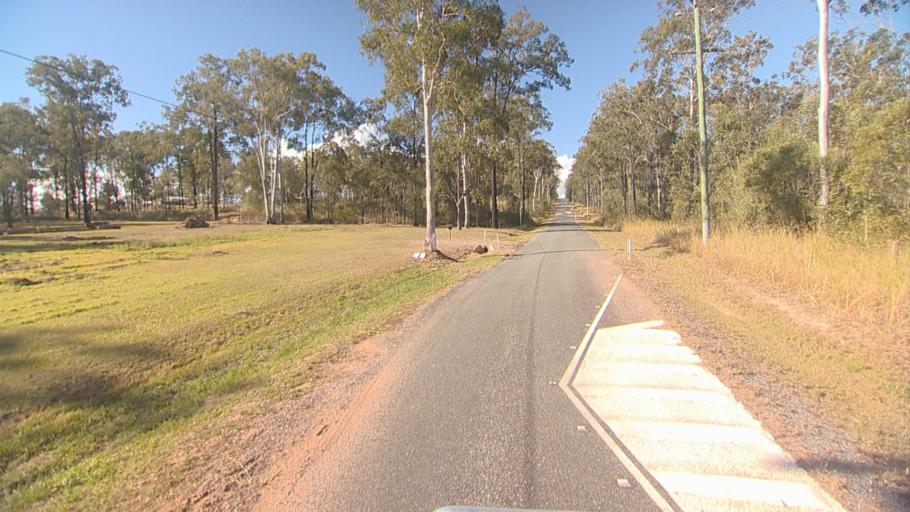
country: AU
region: Queensland
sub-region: Logan
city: Chambers Flat
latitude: -27.7983
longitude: 153.0740
